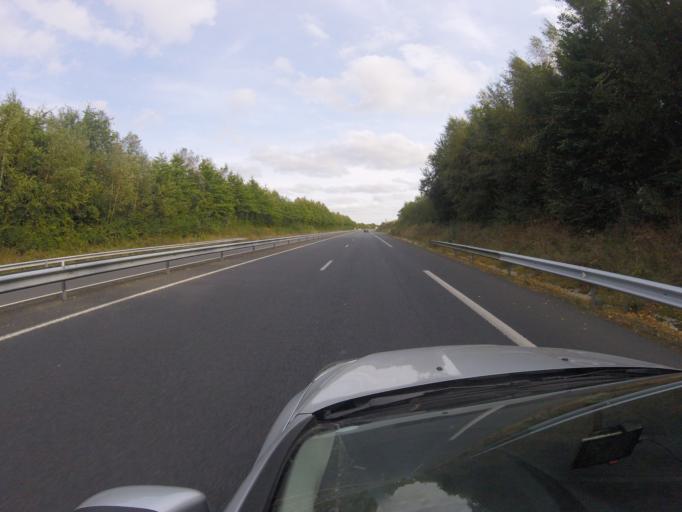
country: FR
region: Lower Normandy
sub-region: Departement de la Manche
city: Pont-Hebert
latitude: 49.1185
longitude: -1.1667
